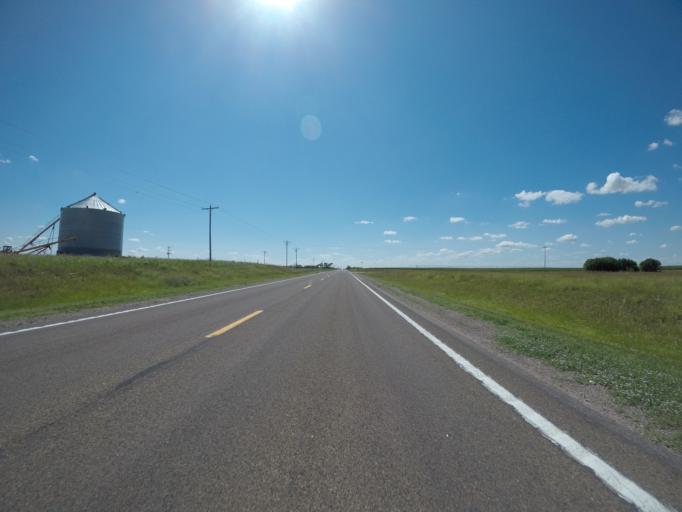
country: US
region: Nebraska
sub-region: Chase County
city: Imperial
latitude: 40.5375
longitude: -101.7784
